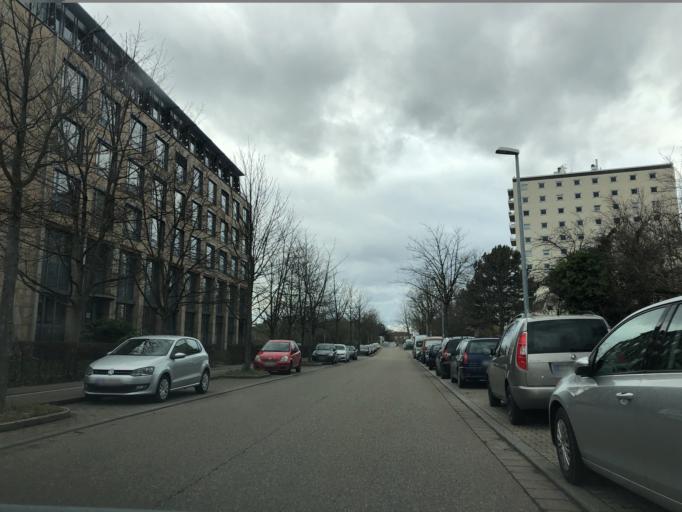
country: DE
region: Baden-Wuerttemberg
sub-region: Freiburg Region
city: Freiburg
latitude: 48.0033
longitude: 7.8319
